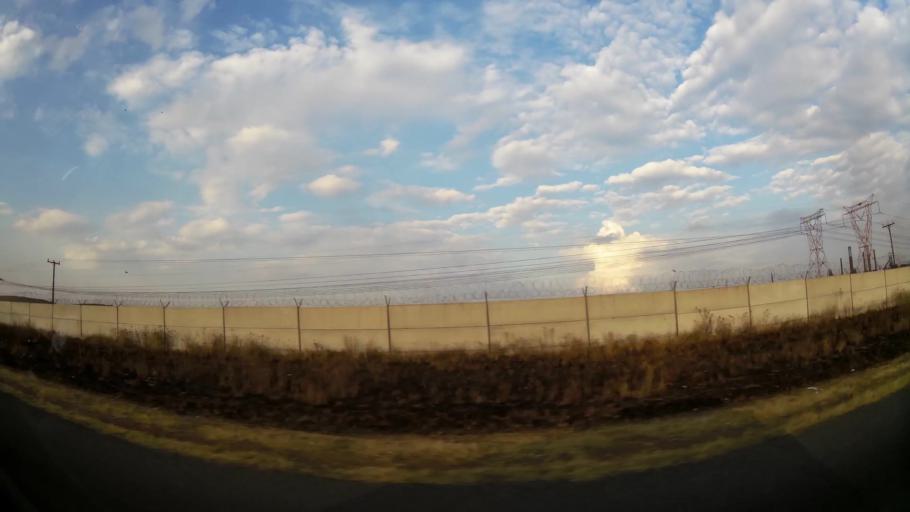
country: ZA
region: Gauteng
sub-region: Sedibeng District Municipality
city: Vanderbijlpark
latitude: -26.6471
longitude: 27.8039
